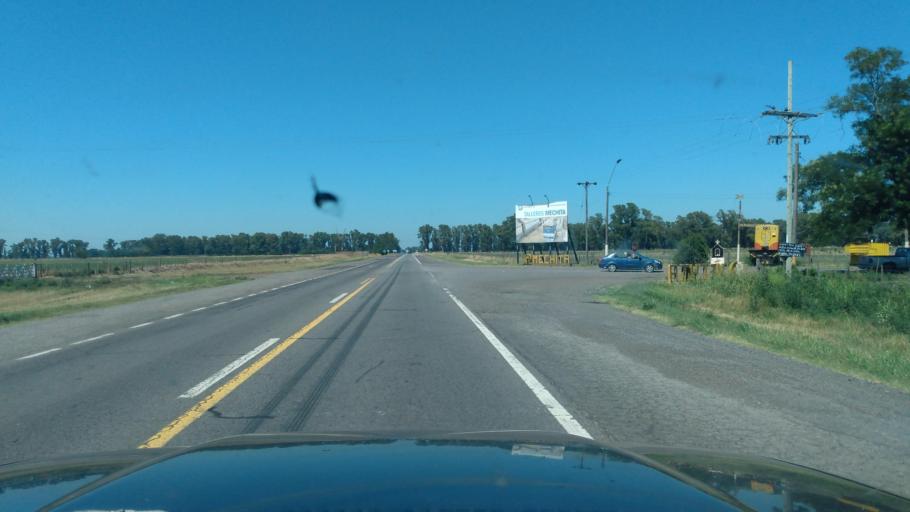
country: AR
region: Buenos Aires
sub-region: Partido de Bragado
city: Bragado
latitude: -35.0912
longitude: -60.3933
